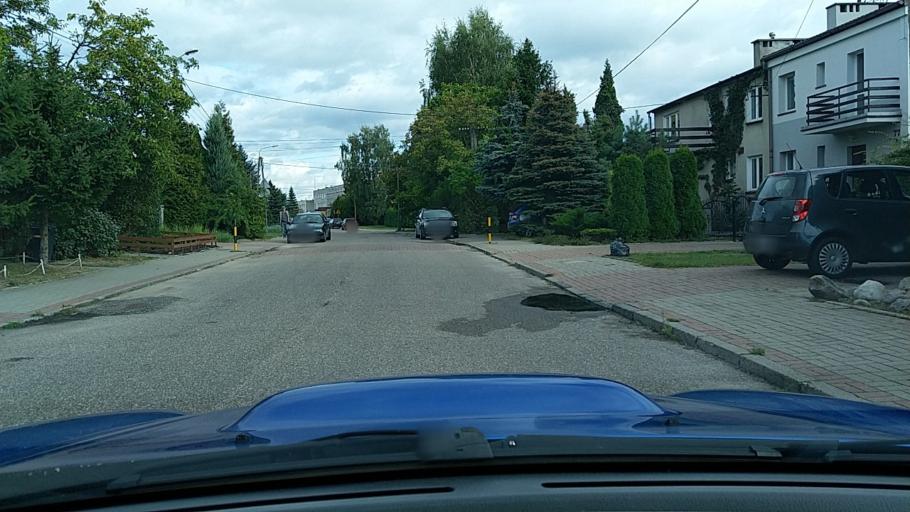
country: PL
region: Warmian-Masurian Voivodeship
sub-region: Olsztyn
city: Kortowo
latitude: 53.7657
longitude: 20.4256
